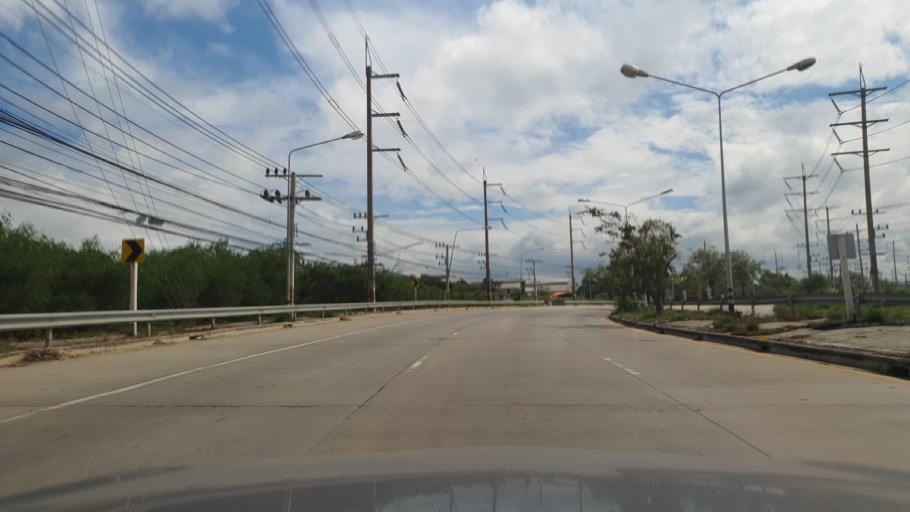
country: TH
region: Chachoengsao
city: Bang Pakong
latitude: 13.5355
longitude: 100.9916
